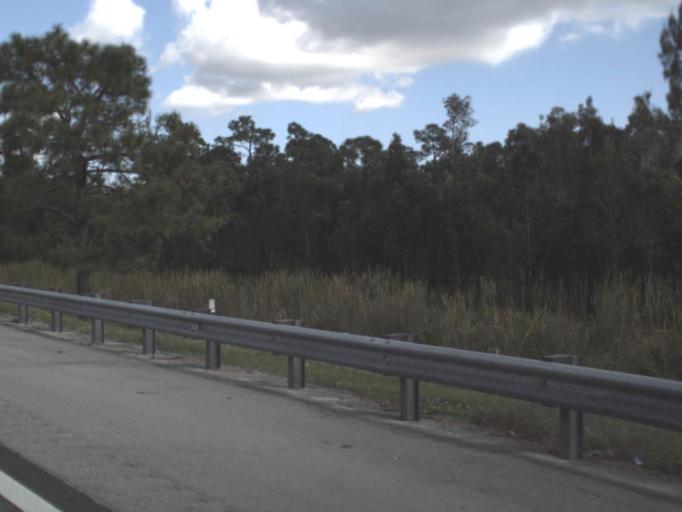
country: US
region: Florida
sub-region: Palm Beach County
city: Schall Circle
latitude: 26.7495
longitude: -80.1344
